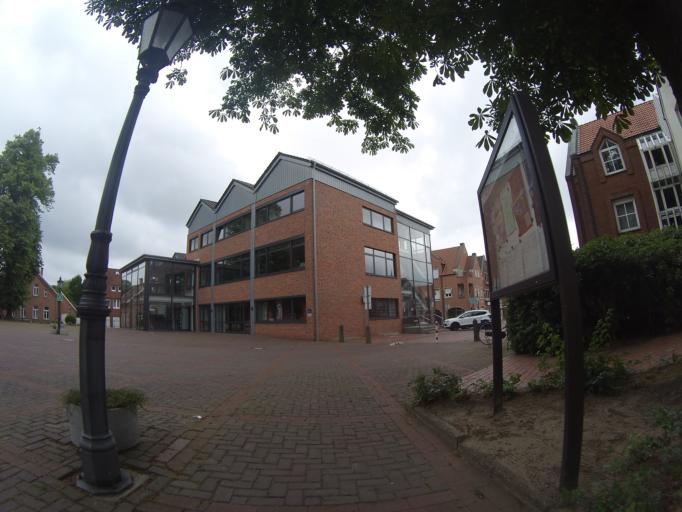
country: DE
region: Lower Saxony
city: Meppen
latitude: 52.6894
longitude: 7.2921
